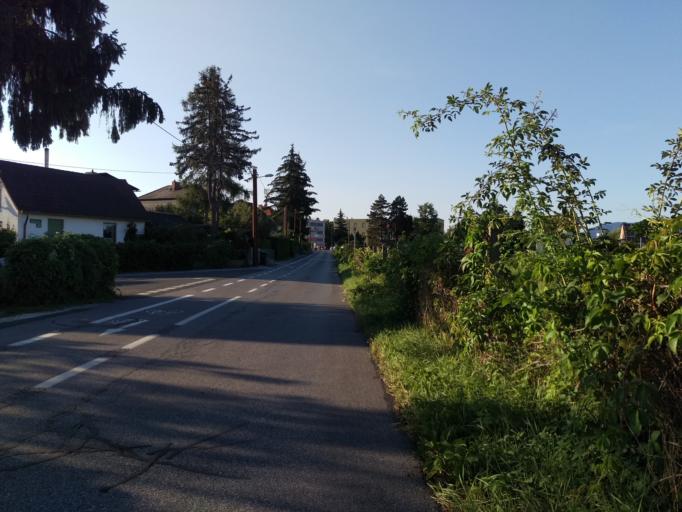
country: AT
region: Styria
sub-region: Graz Stadt
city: Wetzelsdorf
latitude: 47.0531
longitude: 15.4178
